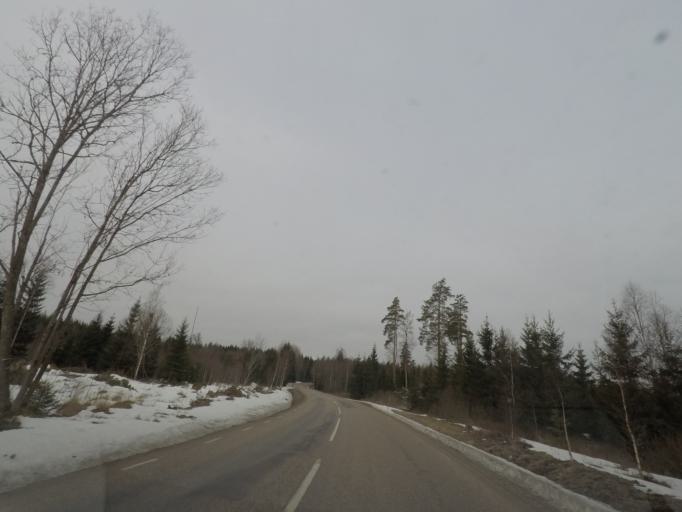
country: SE
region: Vaestmanland
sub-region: Vasteras
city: Skultuna
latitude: 59.7419
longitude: 16.3812
